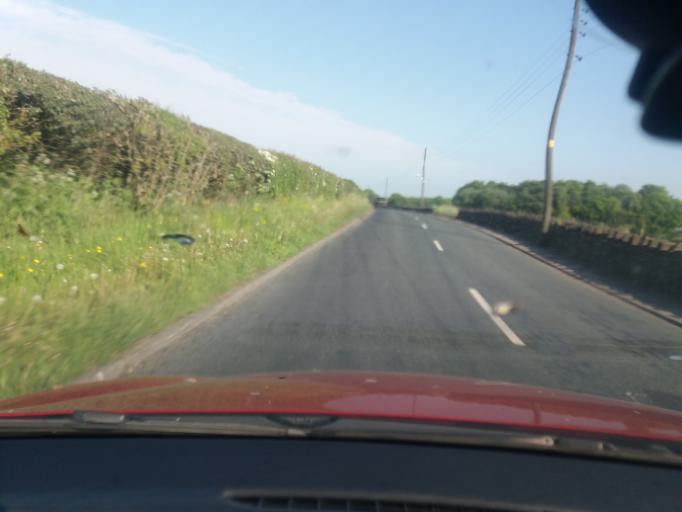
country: GB
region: England
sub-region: Lancashire
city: Adlington
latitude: 53.6321
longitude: -2.5938
